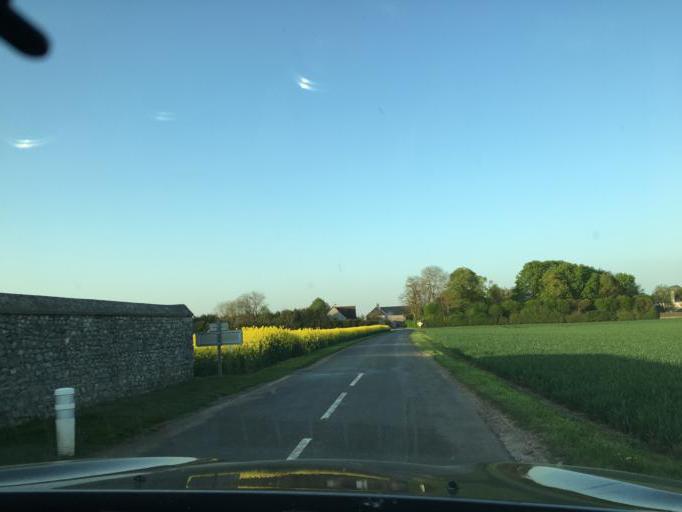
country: FR
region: Centre
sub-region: Departement du Loiret
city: Beaugency
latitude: 47.8009
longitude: 1.5925
